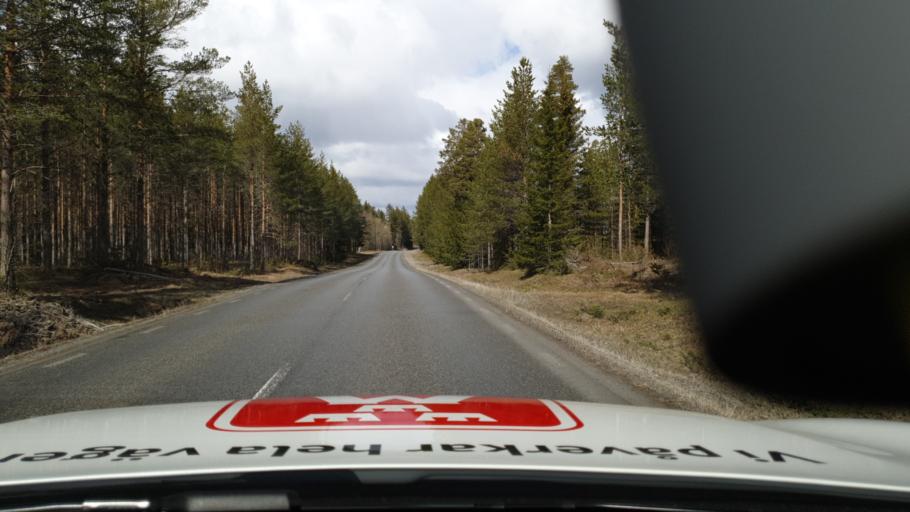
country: SE
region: Jaemtland
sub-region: Krokoms Kommun
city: Krokom
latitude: 63.1342
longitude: 14.2015
